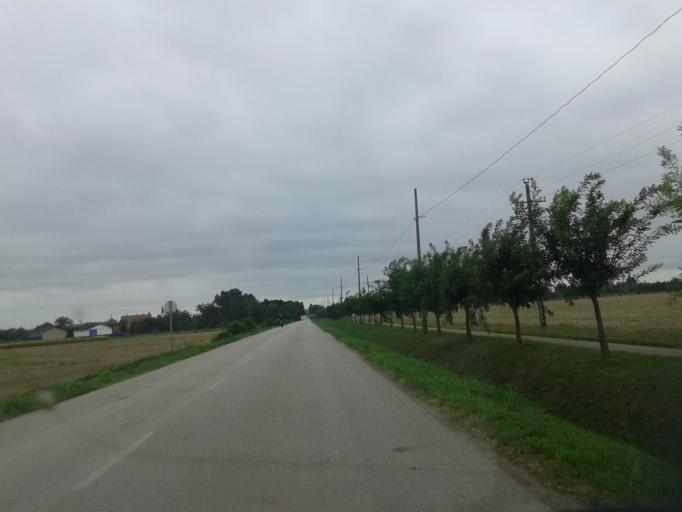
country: HU
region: Bacs-Kiskun
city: Harta
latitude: 46.6948
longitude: 19.0147
